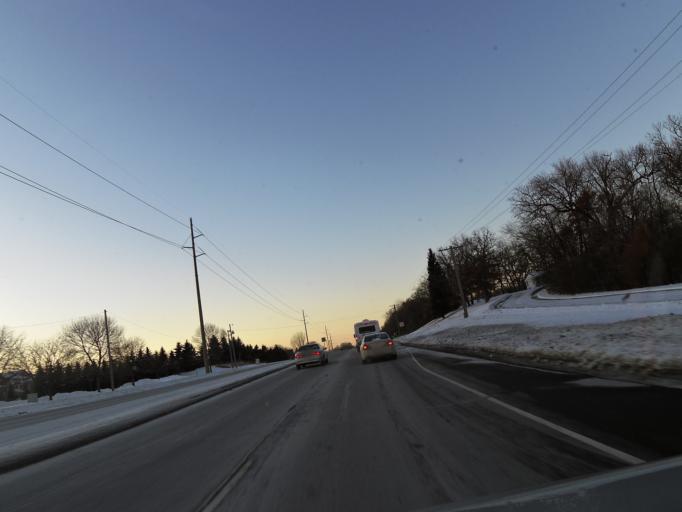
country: US
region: Minnesota
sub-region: Dakota County
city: Apple Valley
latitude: 44.7335
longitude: -93.2534
